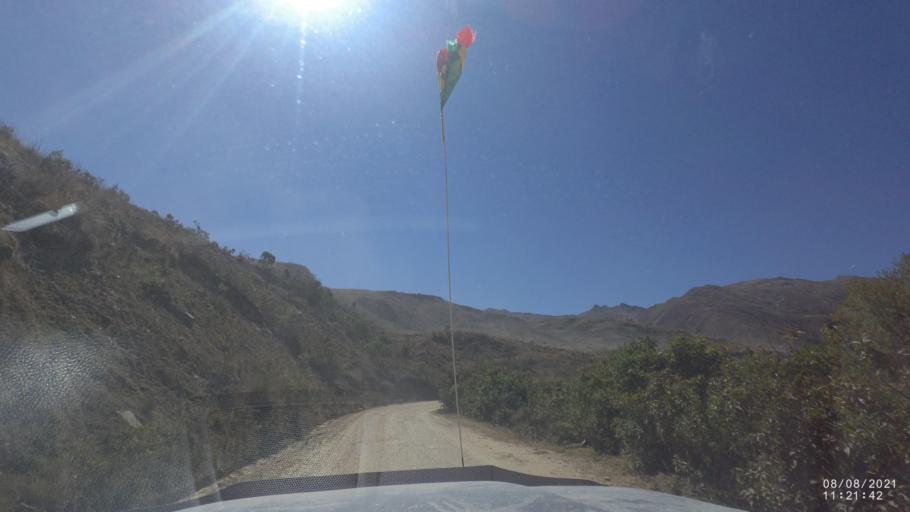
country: BO
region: Cochabamba
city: Colchani
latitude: -16.7781
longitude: -66.6536
